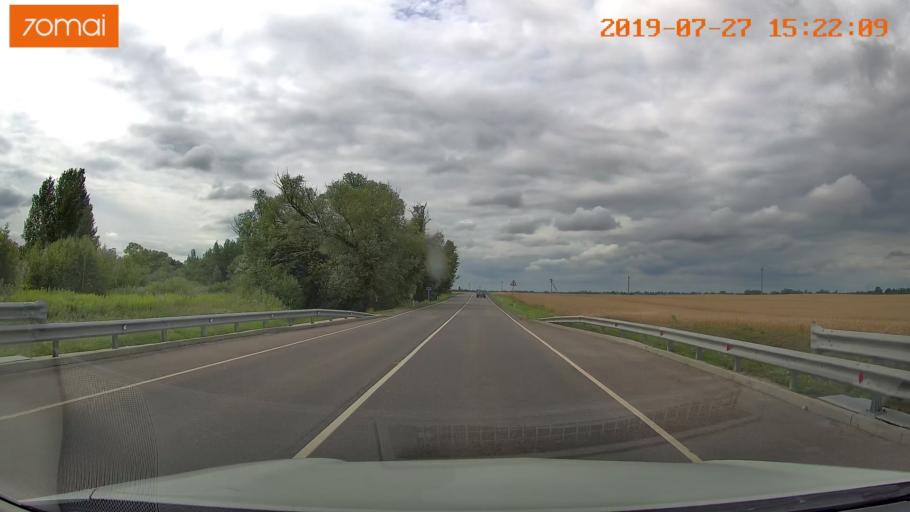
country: RU
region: Kaliningrad
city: Nesterov
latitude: 54.6330
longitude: 22.6663
